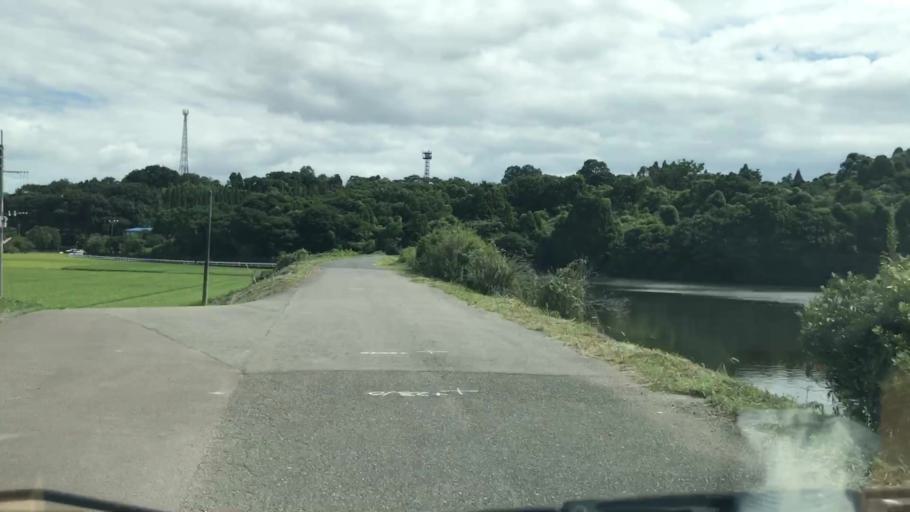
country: JP
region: Saga Prefecture
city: Saga-shi
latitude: 33.2326
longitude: 130.1728
